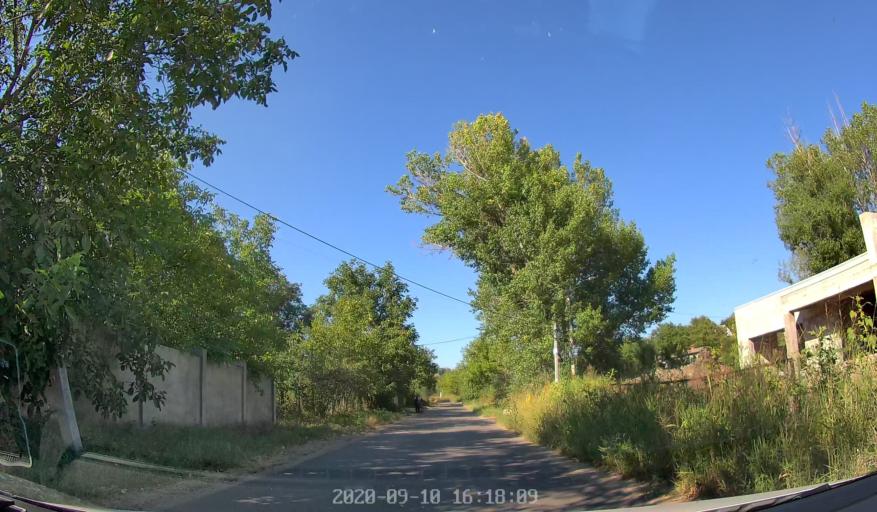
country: MD
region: Chisinau
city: Stauceni
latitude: 47.0515
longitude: 28.9254
